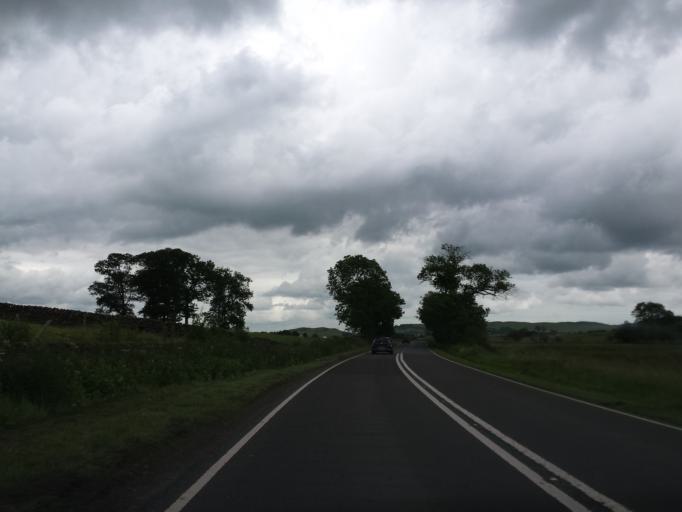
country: GB
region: Scotland
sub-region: Dumfries and Galloway
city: Dalbeattie
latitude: 55.0530
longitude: -3.7560
